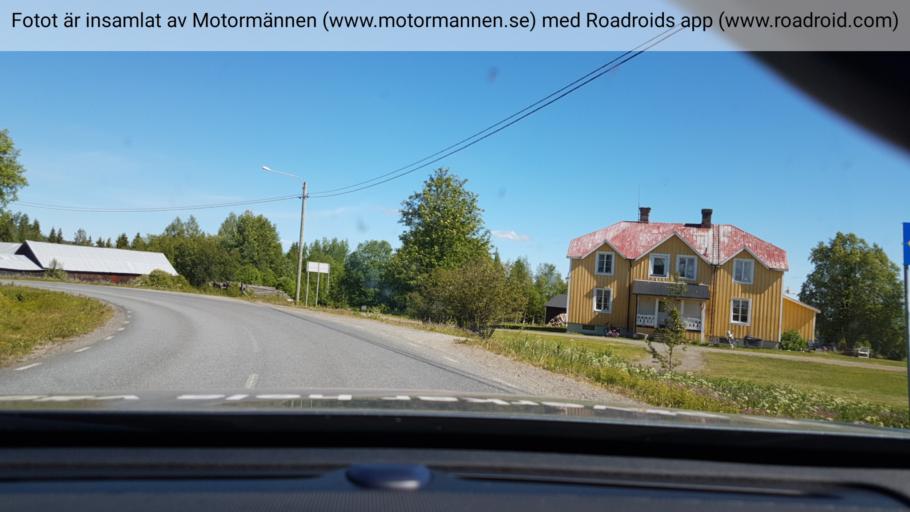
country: SE
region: Vaesterbotten
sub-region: Vilhelmina Kommun
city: Vilhelmina
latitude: 64.6412
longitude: 17.0724
